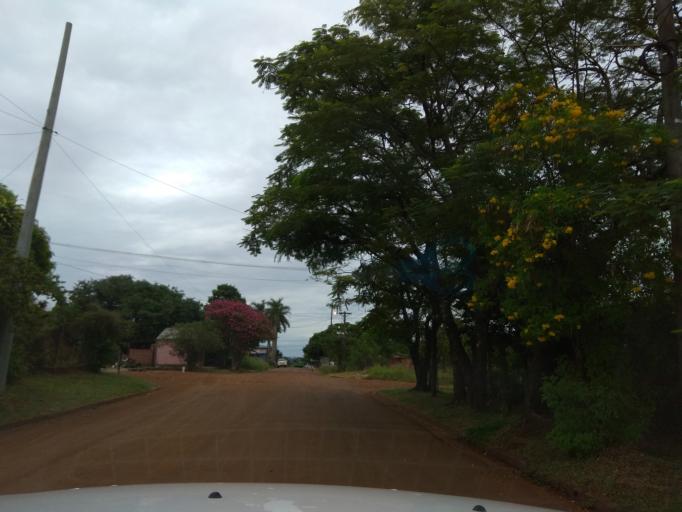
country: AR
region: Misiones
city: Garupa
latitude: -27.4433
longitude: -55.8565
